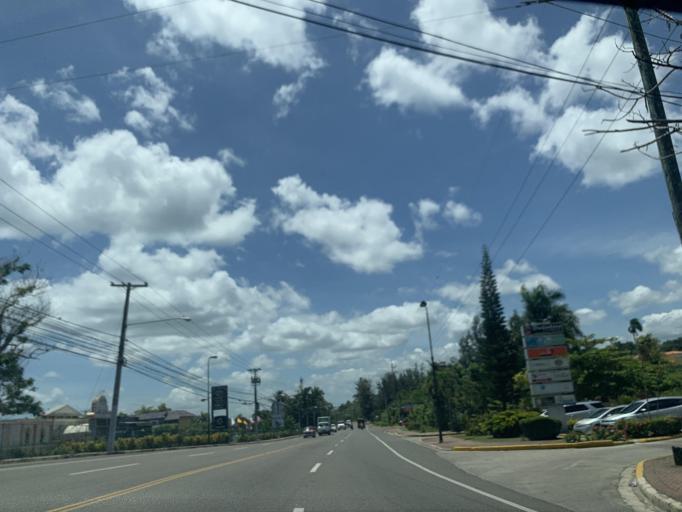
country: DO
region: Puerto Plata
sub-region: Puerto Plata
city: Puerto Plata
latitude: 19.7767
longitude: -70.6607
